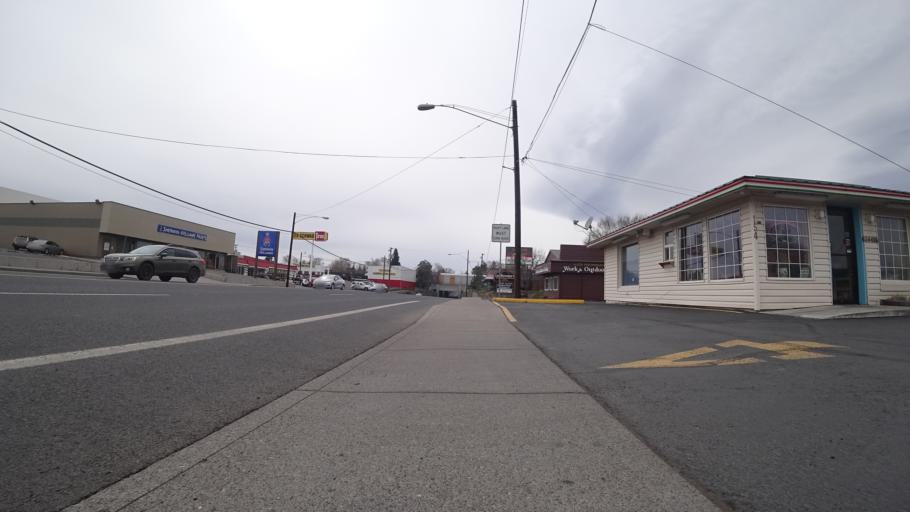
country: US
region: Oregon
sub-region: Deschutes County
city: Bend
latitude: 44.0560
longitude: -121.3047
